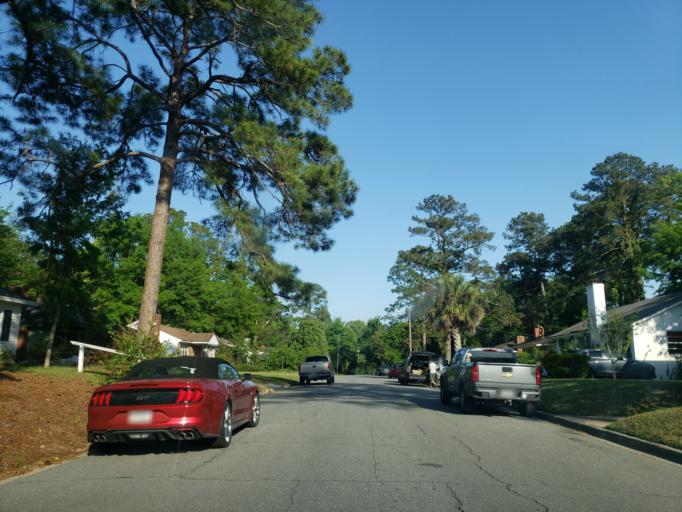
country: US
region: Georgia
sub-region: Chatham County
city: Thunderbolt
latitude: 32.0378
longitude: -81.0810
